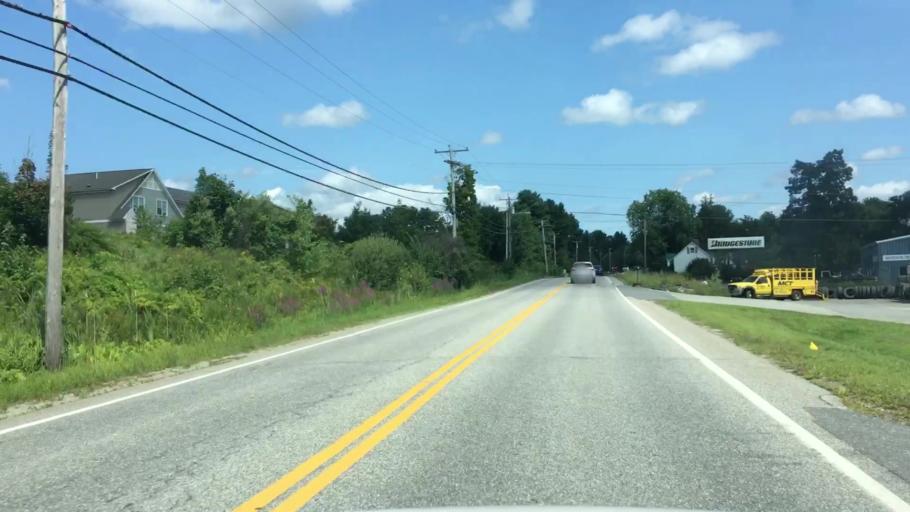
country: US
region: Maine
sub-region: Kennebec County
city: Augusta
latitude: 44.3259
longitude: -69.8178
